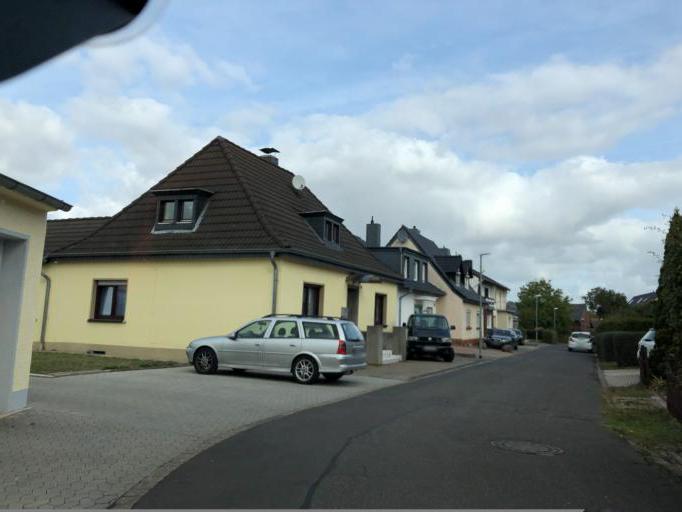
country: DE
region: North Rhine-Westphalia
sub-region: Regierungsbezirk Koln
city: Rheinbach
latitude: 50.6389
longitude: 6.9170
